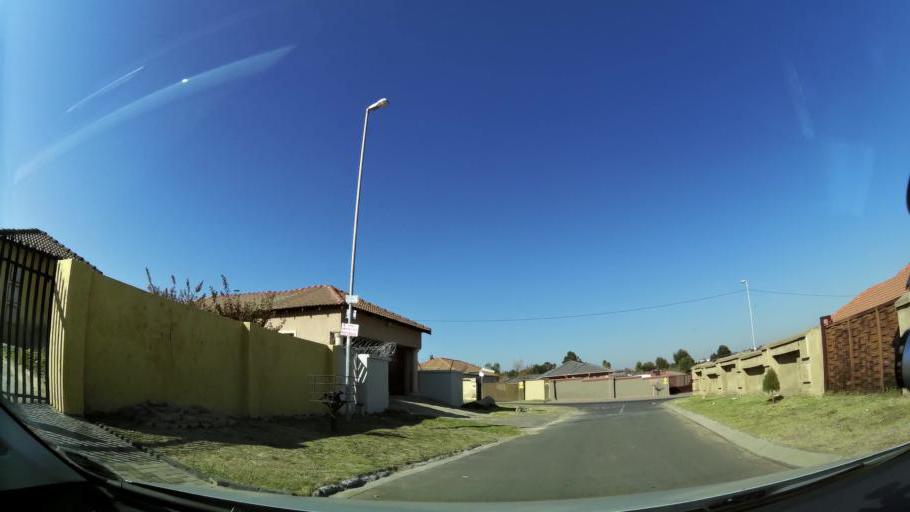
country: ZA
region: Gauteng
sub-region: City of Johannesburg Metropolitan Municipality
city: Modderfontein
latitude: -26.0462
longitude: 28.1972
